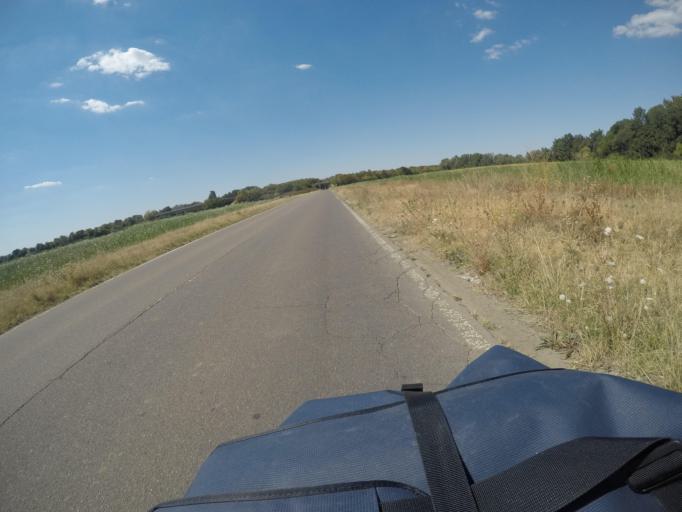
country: DE
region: Rheinland-Pfalz
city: Mutterstadt
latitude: 49.4627
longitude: 8.3656
